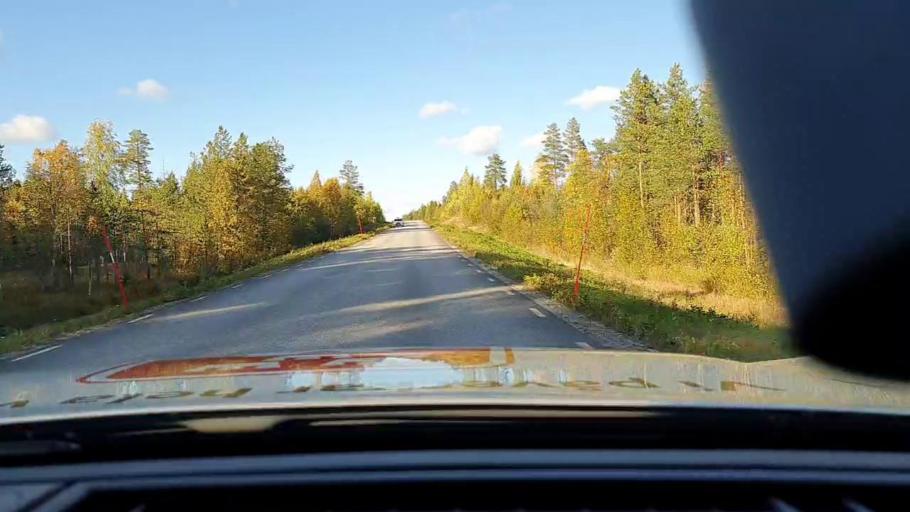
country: SE
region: Norrbotten
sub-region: Pitea Kommun
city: Norrfjarden
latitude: 65.4928
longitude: 21.4735
